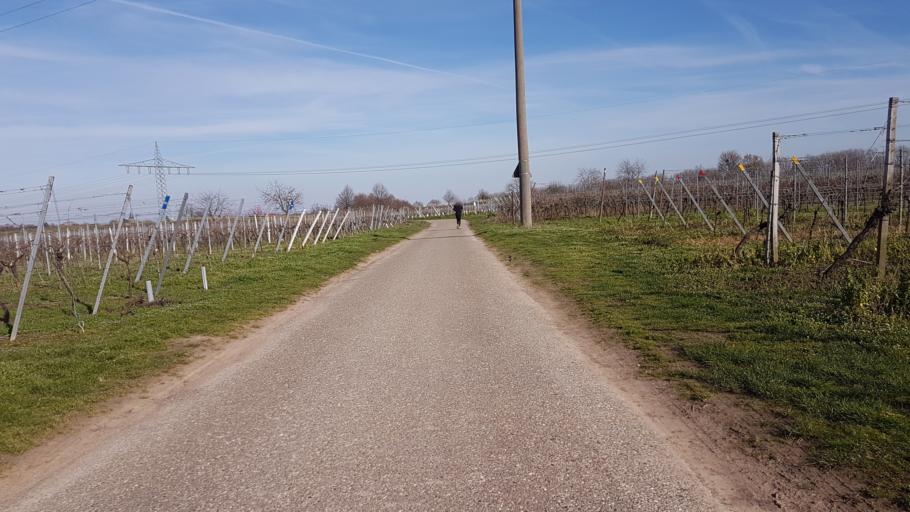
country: DE
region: Rheinland-Pfalz
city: Maikammer
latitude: 49.2957
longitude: 8.1456
